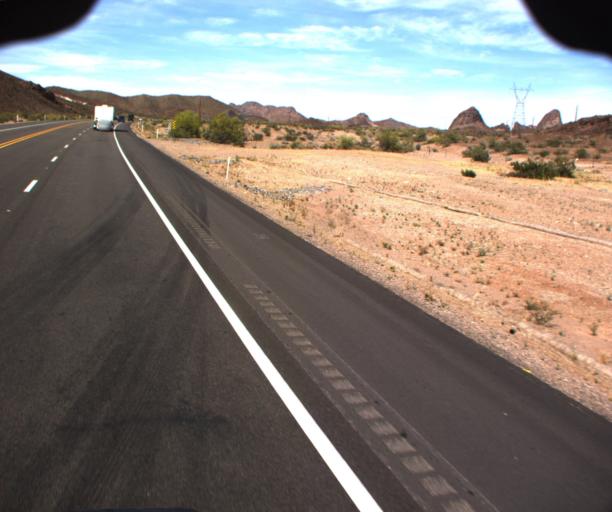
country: US
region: Arizona
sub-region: Mohave County
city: Desert Hills
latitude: 34.5920
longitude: -114.3696
